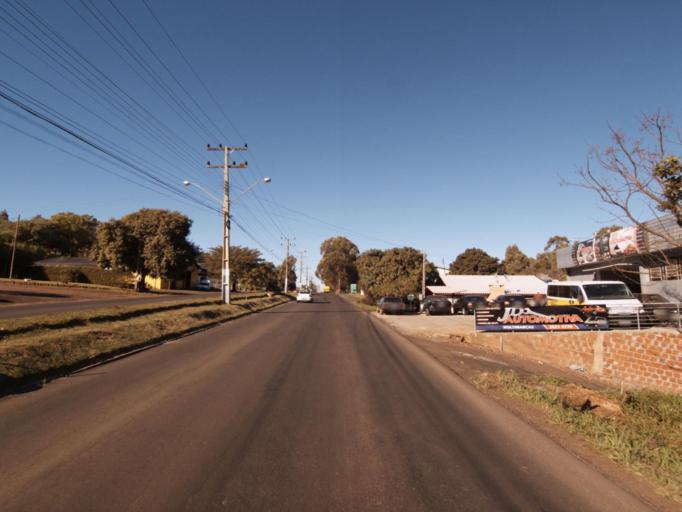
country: AR
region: Misiones
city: Bernardo de Irigoyen
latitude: -26.7481
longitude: -53.5010
